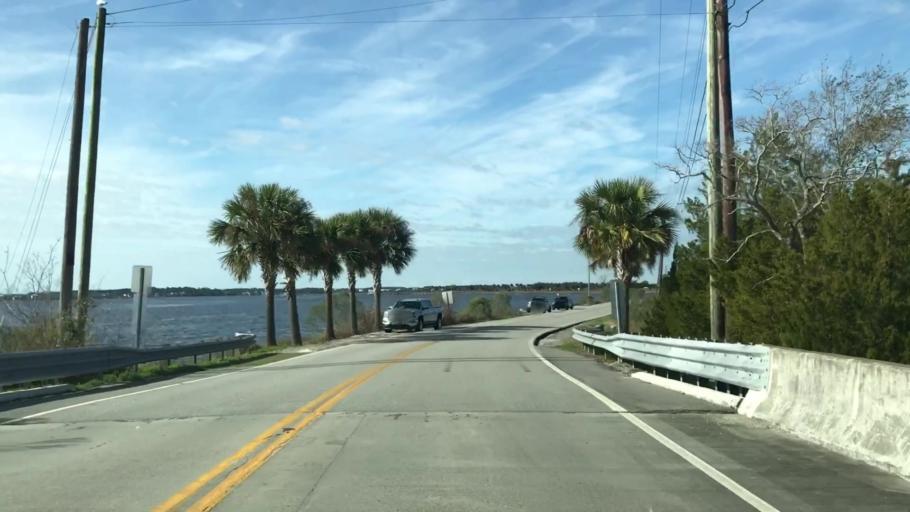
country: US
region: South Carolina
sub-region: Charleston County
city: Charleston
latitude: 32.7719
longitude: -80.0074
